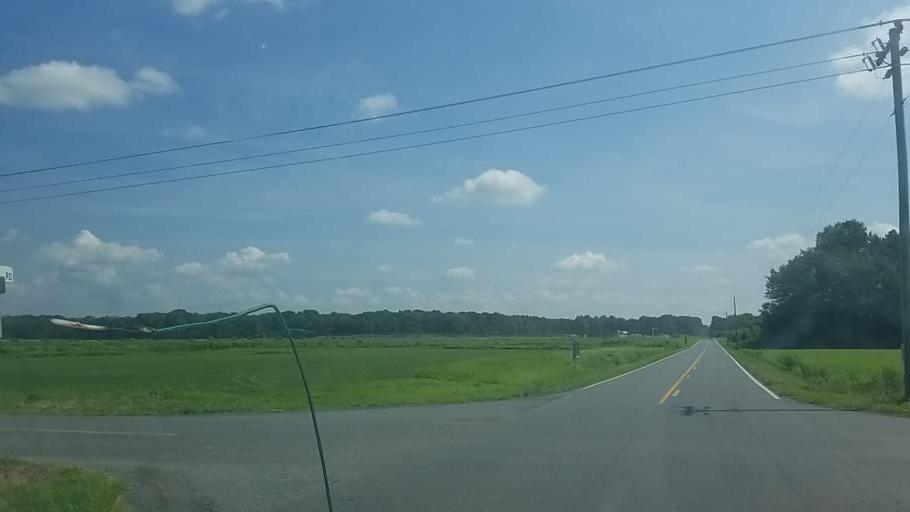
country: US
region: Maryland
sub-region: Wicomico County
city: Hebron
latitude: 38.4321
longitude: -75.6979
